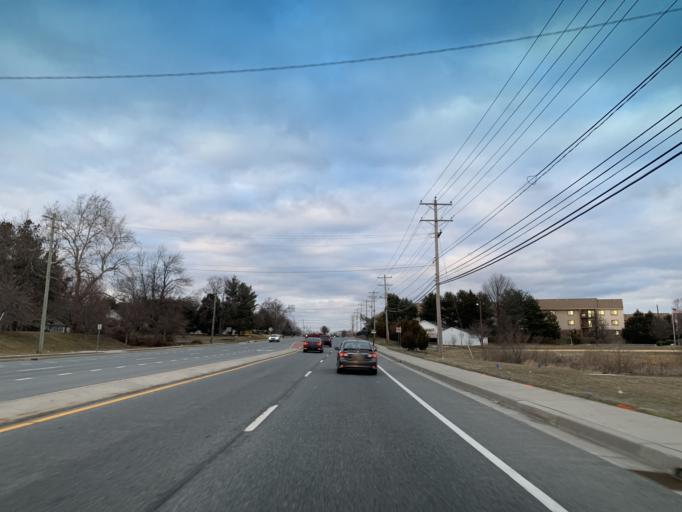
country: US
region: Delaware
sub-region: New Castle County
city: Bear
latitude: 39.6506
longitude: -75.6558
